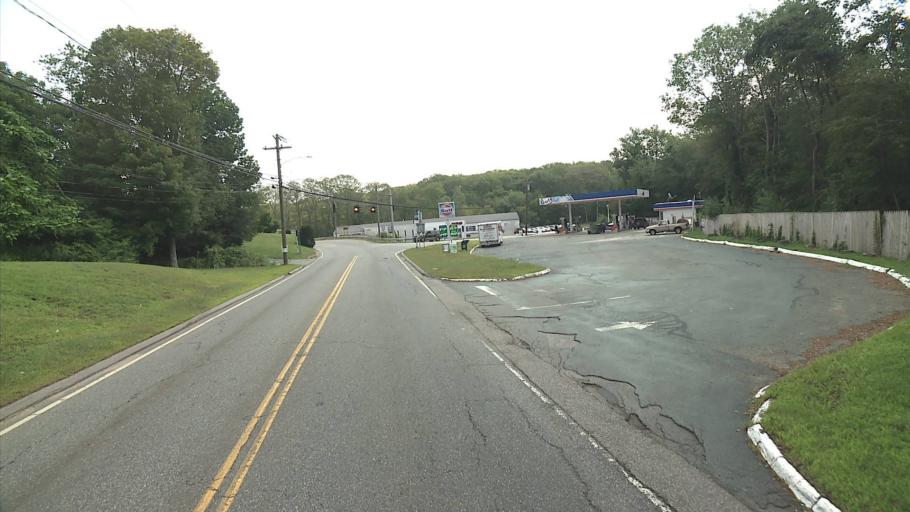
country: US
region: Connecticut
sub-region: New London County
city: Montville Center
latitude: 41.5021
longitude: -72.2022
